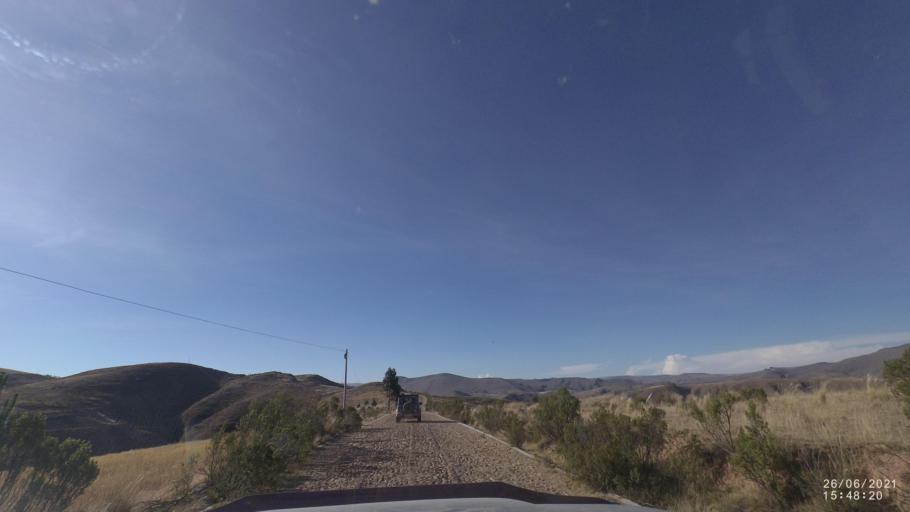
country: BO
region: Cochabamba
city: Arani
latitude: -17.8639
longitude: -65.6964
